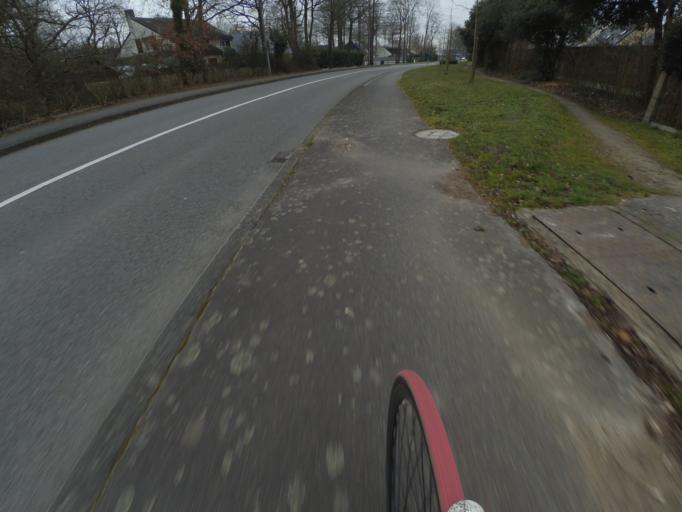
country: FR
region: Pays de la Loire
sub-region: Departement de la Loire-Atlantique
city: Sainte-Luce-sur-Loire
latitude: 47.2737
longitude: -1.4834
